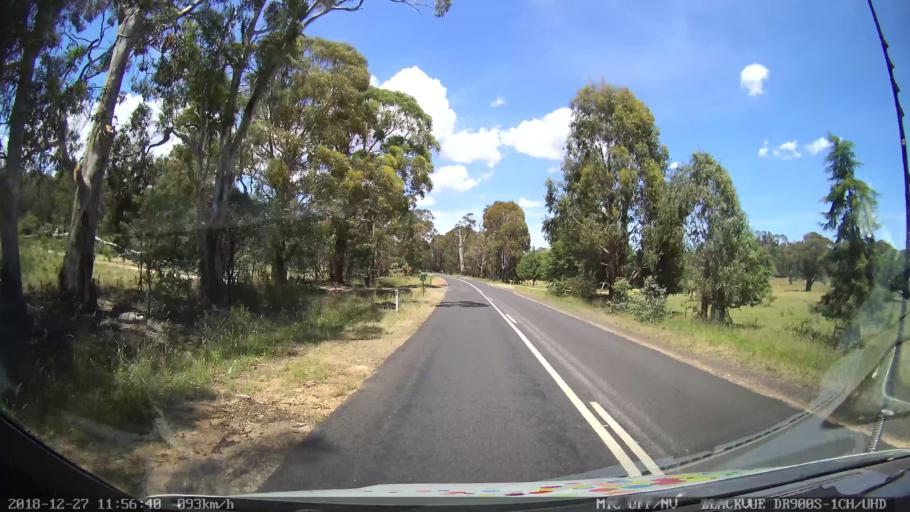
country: AU
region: New South Wales
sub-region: Blayney
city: Blayney
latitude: -33.7011
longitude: 149.3892
